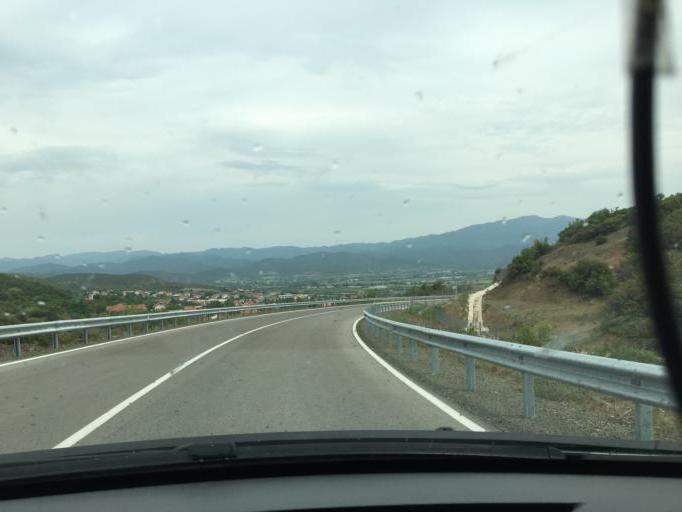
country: MK
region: Gevgelija
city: Miravci
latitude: 41.3008
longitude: 22.4326
